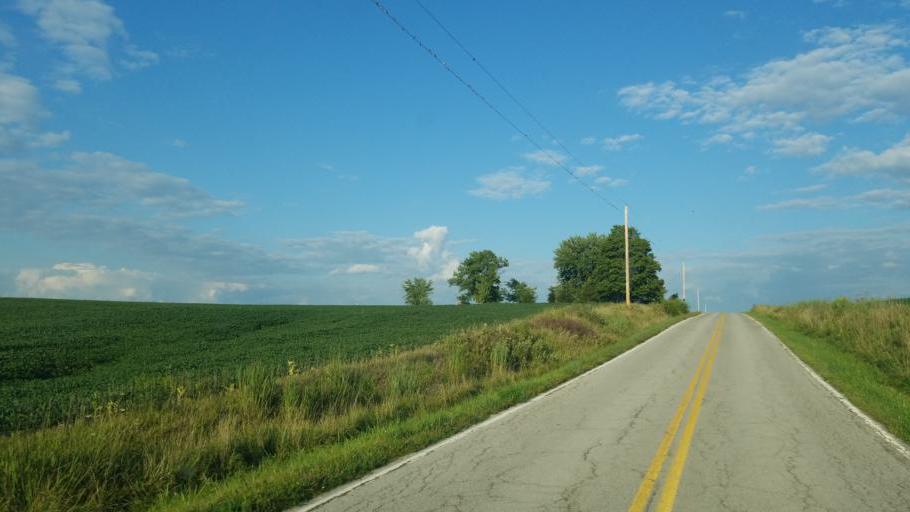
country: US
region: Ohio
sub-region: Huron County
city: Willard
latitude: 41.1096
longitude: -82.8284
